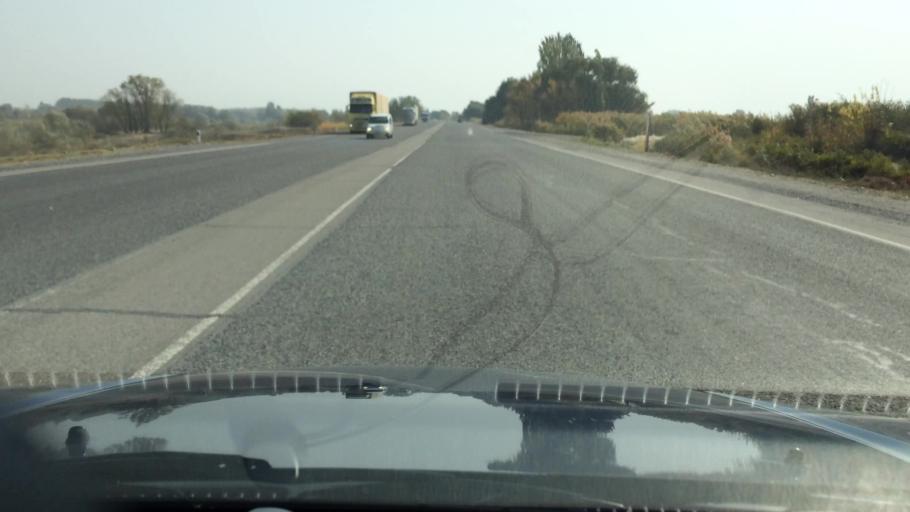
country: KG
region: Chuy
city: Kant
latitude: 42.9441
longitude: 74.9628
